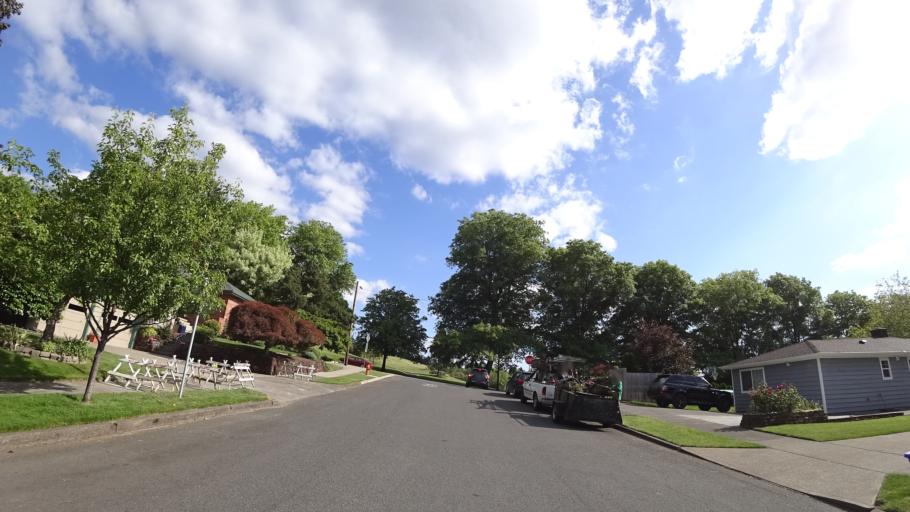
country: US
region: Oregon
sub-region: Washington County
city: Garden Home-Whitford
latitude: 45.4766
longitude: -122.7210
